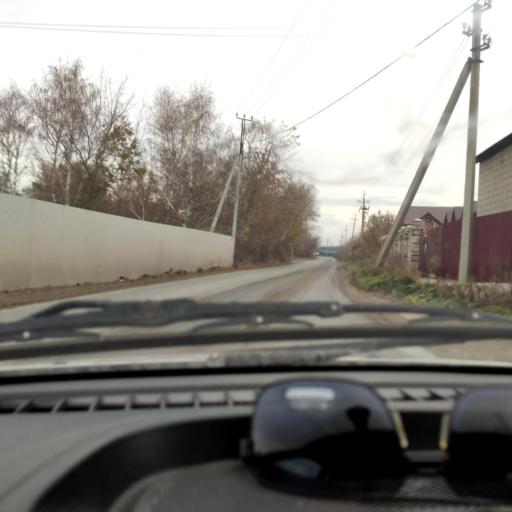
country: RU
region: Samara
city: Zhigulevsk
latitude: 53.5218
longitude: 49.4862
